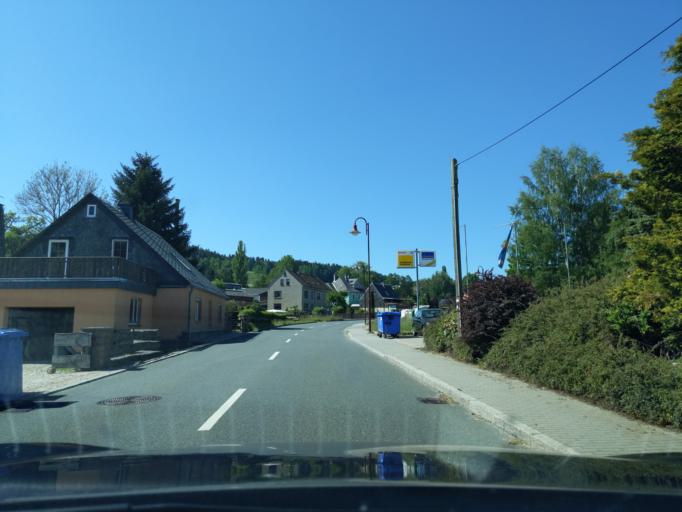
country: DE
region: Saxony
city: Stutzengrun
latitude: 50.5743
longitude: 12.5414
